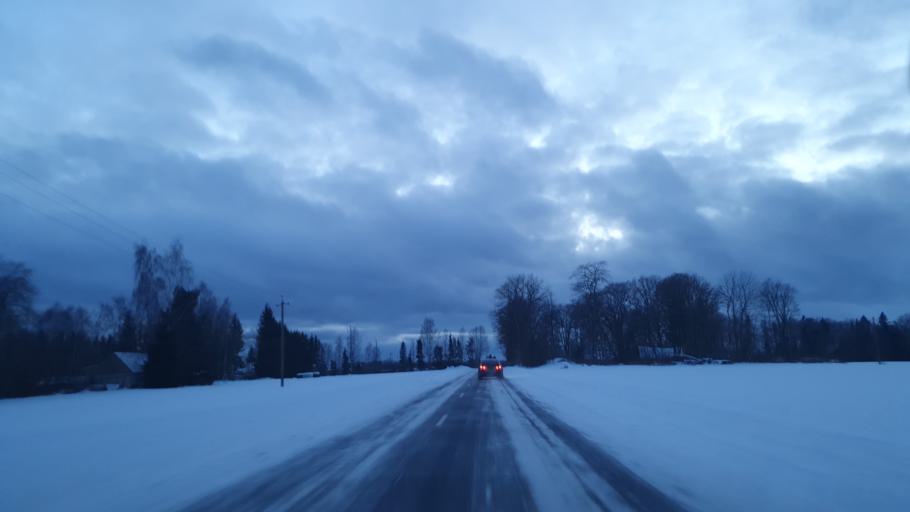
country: EE
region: Jogevamaa
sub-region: Jogeva linn
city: Jogeva
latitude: 58.5846
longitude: 26.3182
